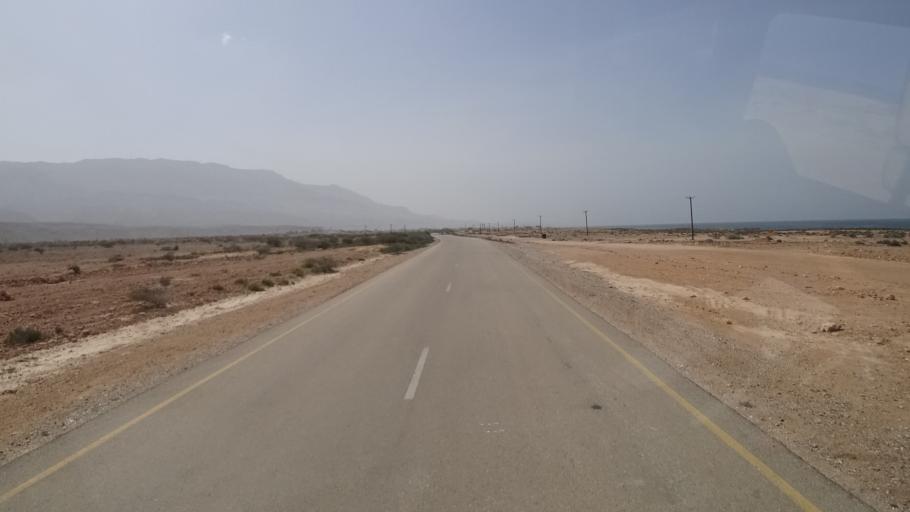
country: OM
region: Ash Sharqiyah
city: Sur
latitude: 22.9811
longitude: 59.1523
